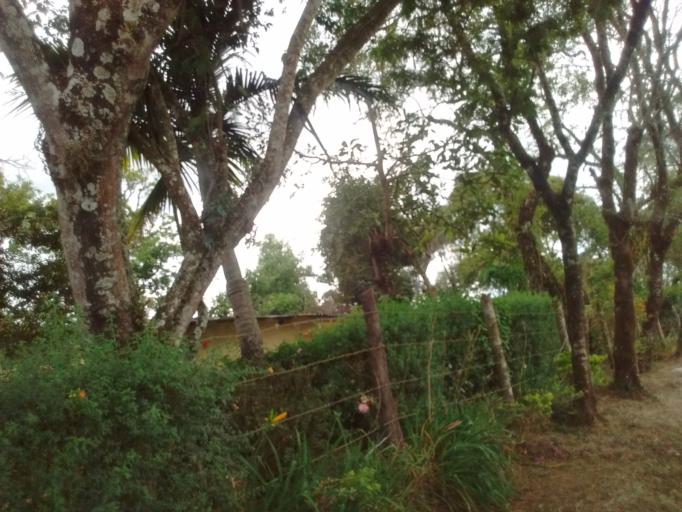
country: CO
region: Cauca
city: Popayan
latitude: 2.4509
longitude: -76.5214
